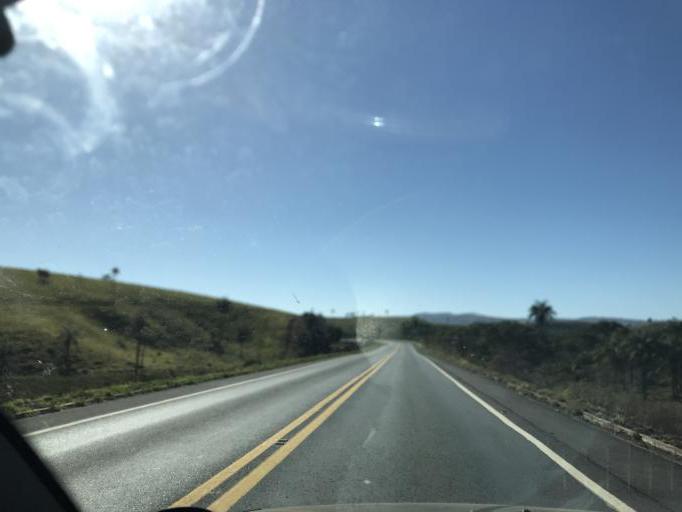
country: BR
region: Minas Gerais
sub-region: Bambui
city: Bambui
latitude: -19.8365
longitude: -46.0026
